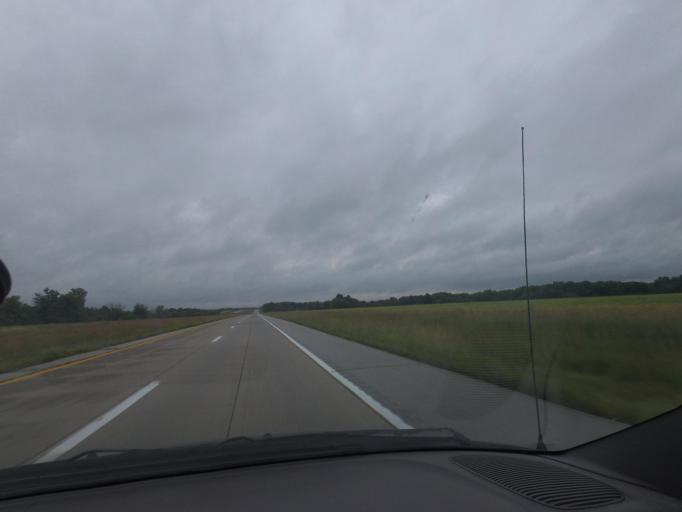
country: US
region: Missouri
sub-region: Marion County
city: Monroe City
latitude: 39.6581
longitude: -91.7812
